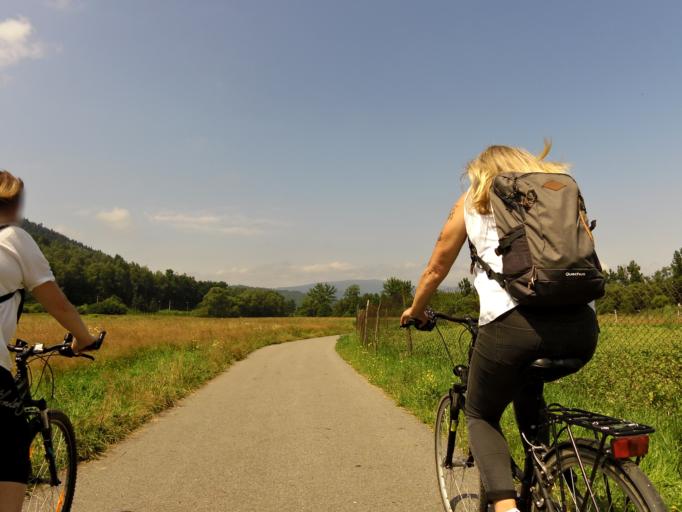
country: PL
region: Silesian Voivodeship
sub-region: Powiat zywiecki
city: Milowka
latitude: 49.5384
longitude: 19.1071
